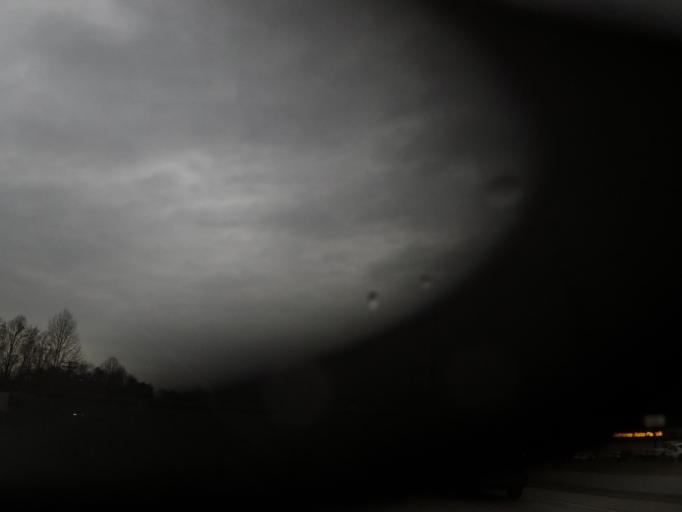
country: US
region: South Carolina
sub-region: Greenville County
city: Travelers Rest
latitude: 34.9691
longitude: -82.4290
